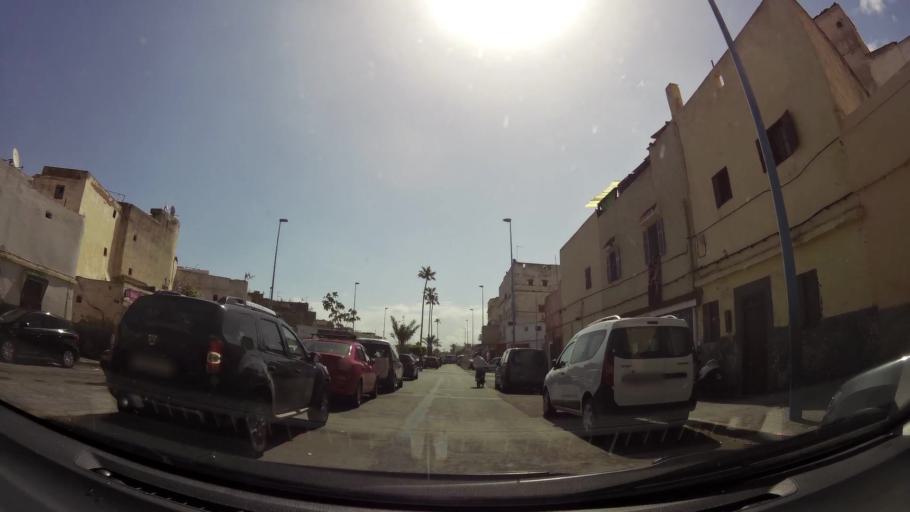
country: MA
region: Grand Casablanca
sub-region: Casablanca
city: Casablanca
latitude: 33.6072
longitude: -7.6284
